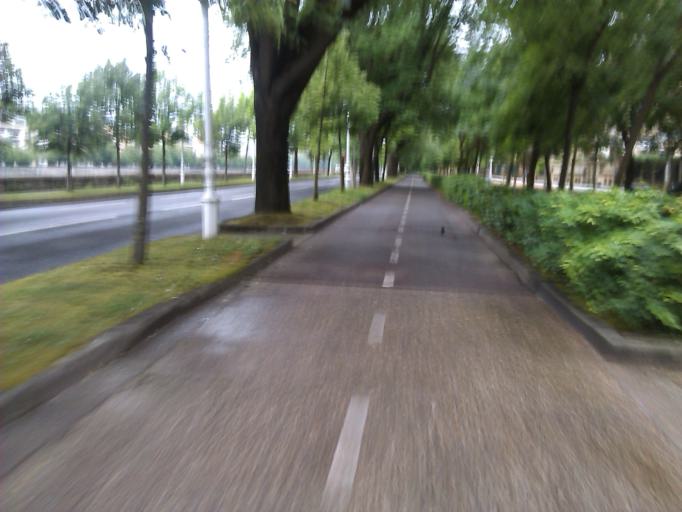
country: ES
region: Basque Country
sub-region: Provincia de Guipuzcoa
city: San Sebastian
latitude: 43.3168
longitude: -1.9792
